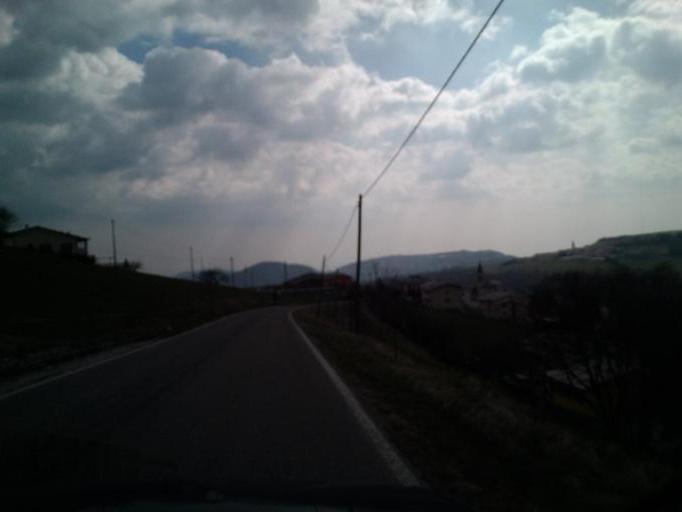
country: IT
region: Veneto
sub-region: Provincia di Verona
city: Sant'Anna d'Alfaedo
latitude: 45.6422
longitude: 10.9645
